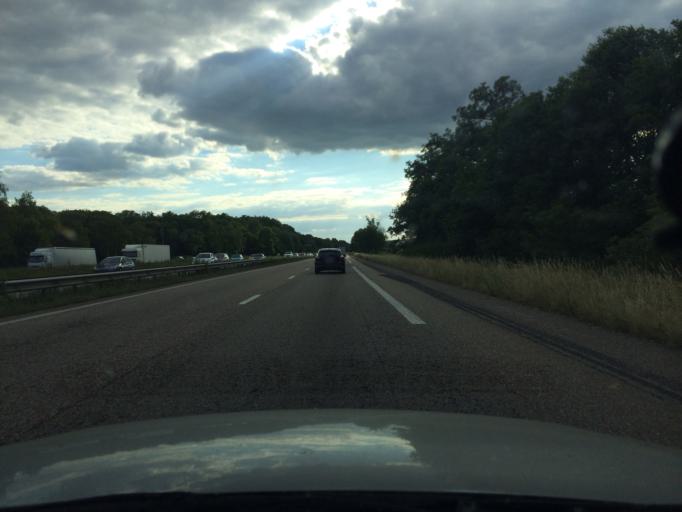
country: FR
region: Lorraine
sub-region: Departement de Meurthe-et-Moselle
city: Velaine-en-Haye
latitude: 48.6888
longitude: 6.0131
